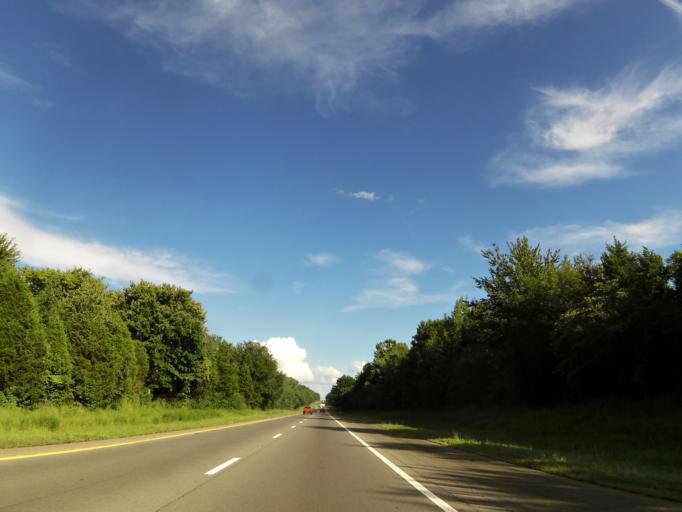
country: US
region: Tennessee
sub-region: Cheatham County
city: Pleasant View
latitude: 36.4274
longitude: -87.0656
